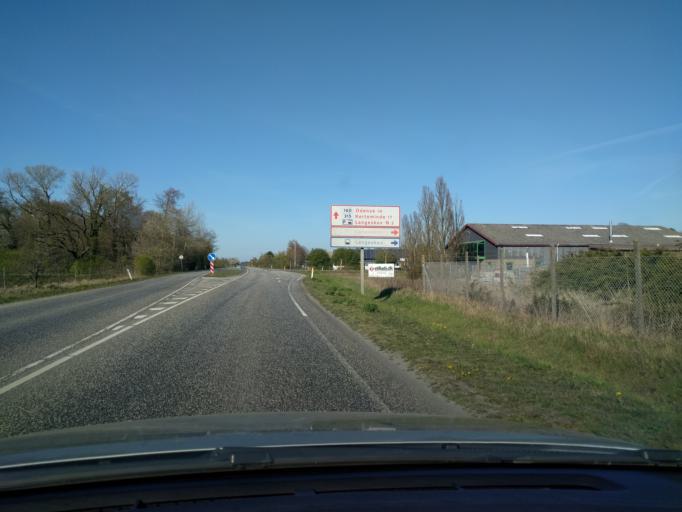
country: DK
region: South Denmark
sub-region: Kerteminde Kommune
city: Langeskov
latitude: 55.3569
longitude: 10.5803
